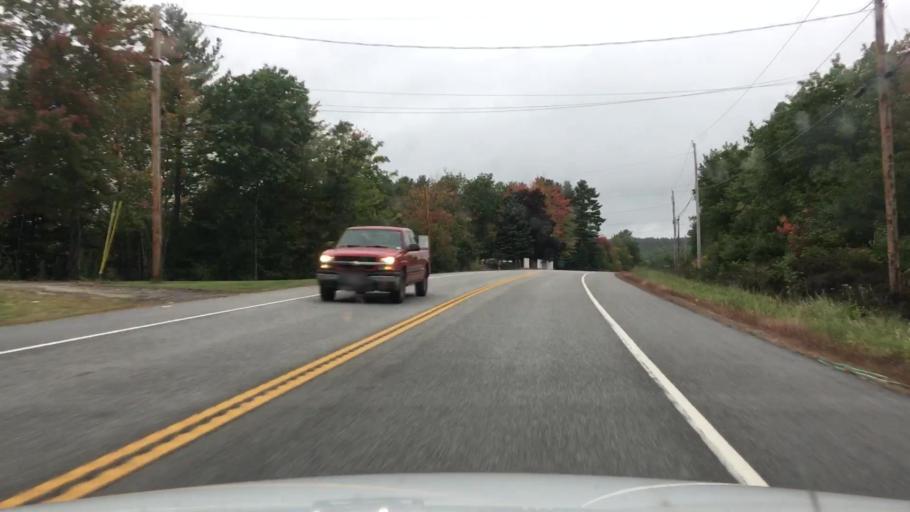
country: US
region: Maine
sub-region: Androscoggin County
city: Poland
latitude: 44.0478
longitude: -70.3801
